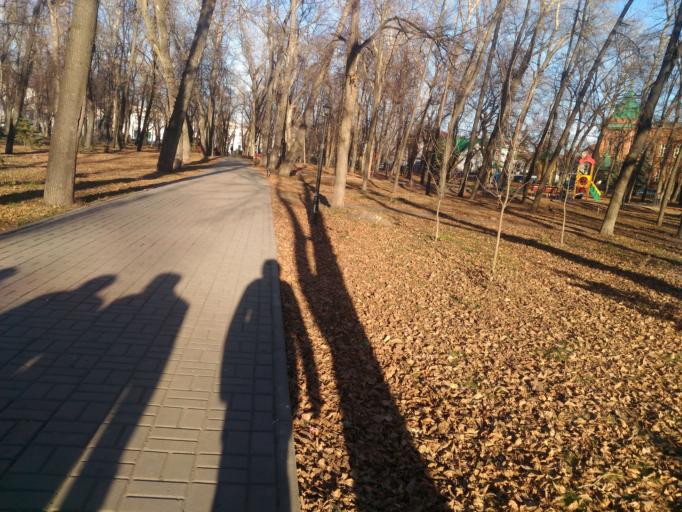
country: RU
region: Ulyanovsk
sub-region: Ulyanovskiy Rayon
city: Ulyanovsk
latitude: 54.3091
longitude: 48.3792
